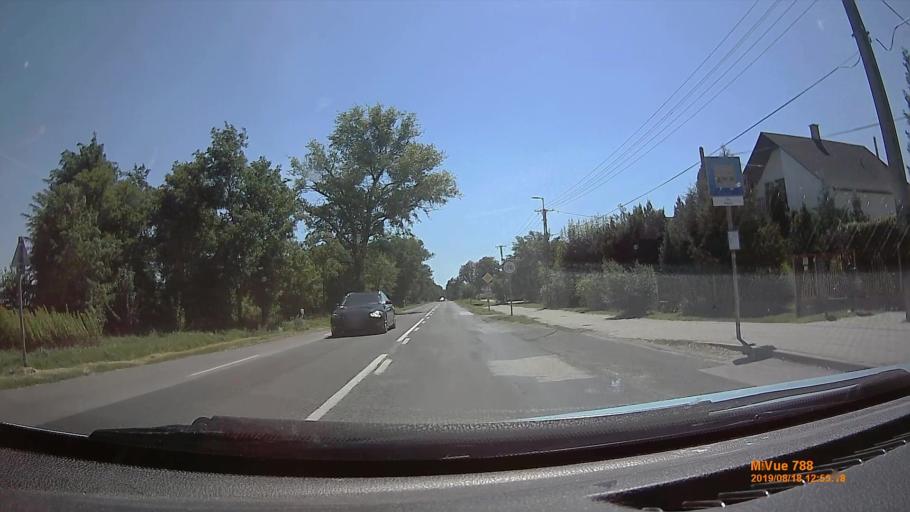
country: HU
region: Fejer
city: Aba
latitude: 47.0353
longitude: 18.5359
